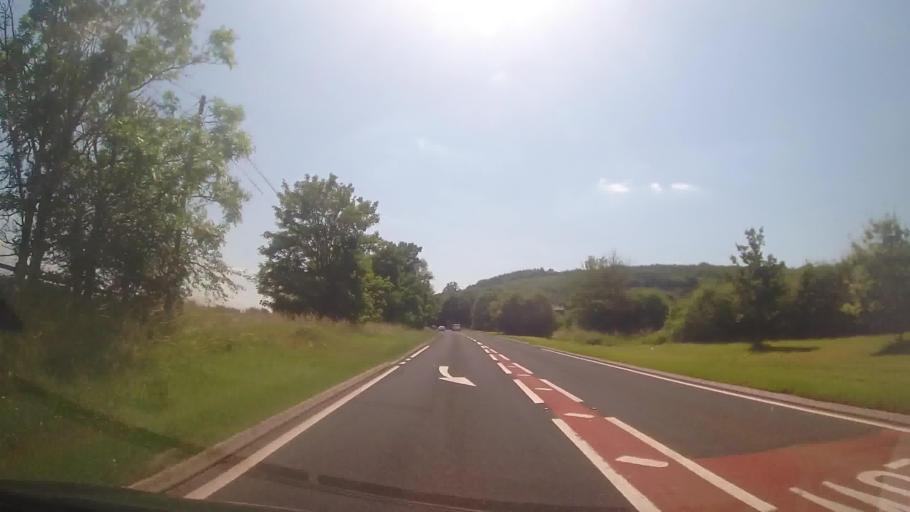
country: GB
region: England
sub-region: Herefordshire
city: Ocle Pychard
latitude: 52.0913
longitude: -2.5808
